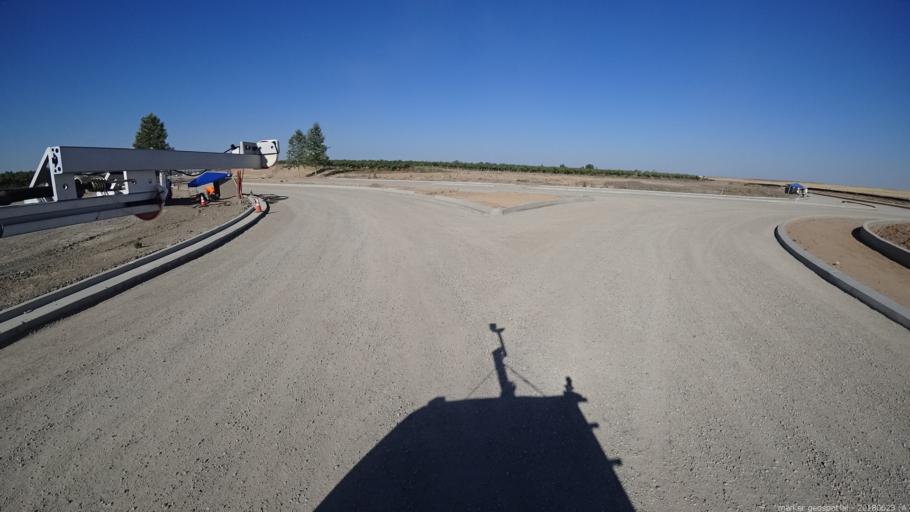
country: US
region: California
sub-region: Madera County
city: Bonadelle Ranchos-Madera Ranchos
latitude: 36.9663
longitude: -119.7840
